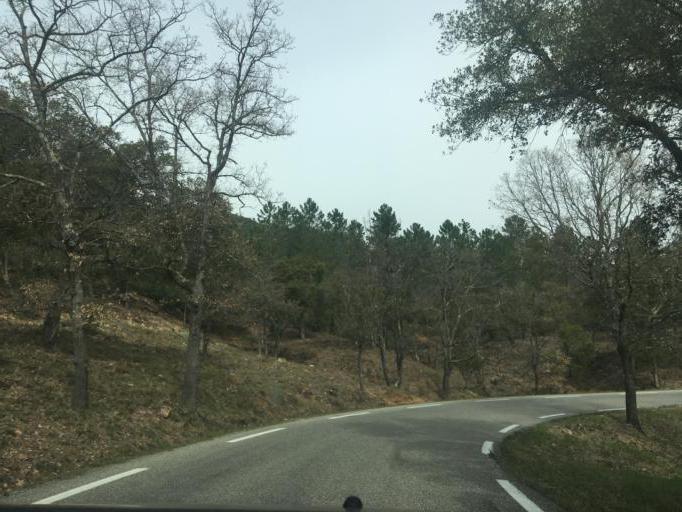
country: FR
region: Provence-Alpes-Cote d'Azur
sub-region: Departement du Var
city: Bagnols-en-Foret
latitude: 43.5270
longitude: 6.6522
